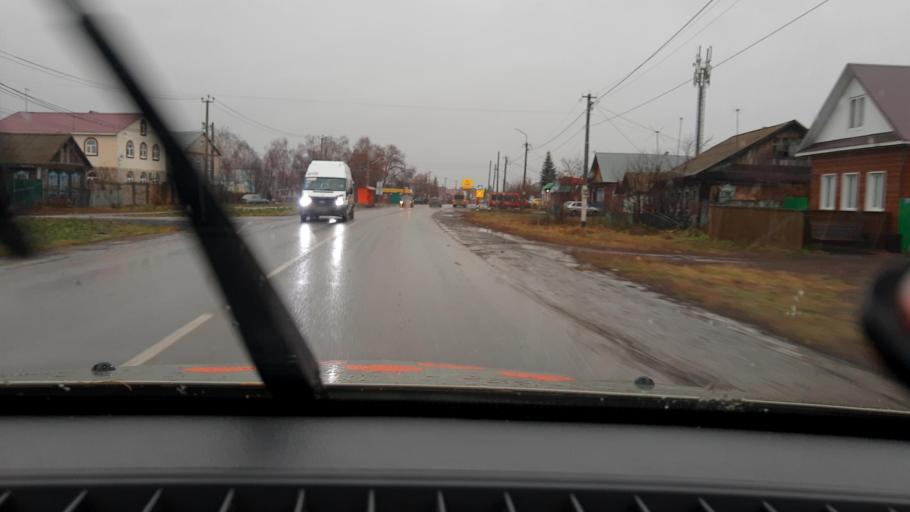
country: RU
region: Bashkortostan
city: Ufa
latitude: 54.6139
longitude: 55.9015
